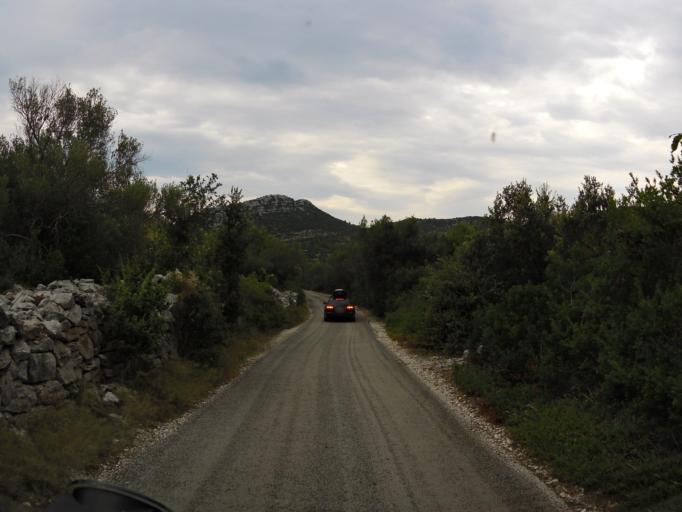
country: HR
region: Zadarska
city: Sali
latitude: 43.9353
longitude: 15.1456
